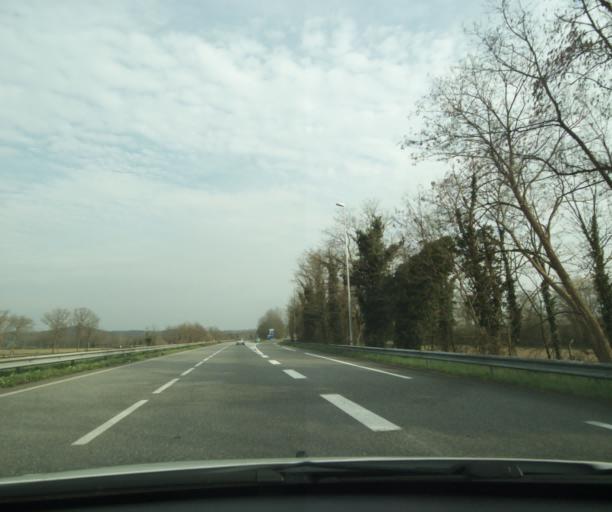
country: FR
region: Aquitaine
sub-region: Departement des Pyrenees-Atlantiques
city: Mourenx
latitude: 43.4228
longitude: -0.6031
